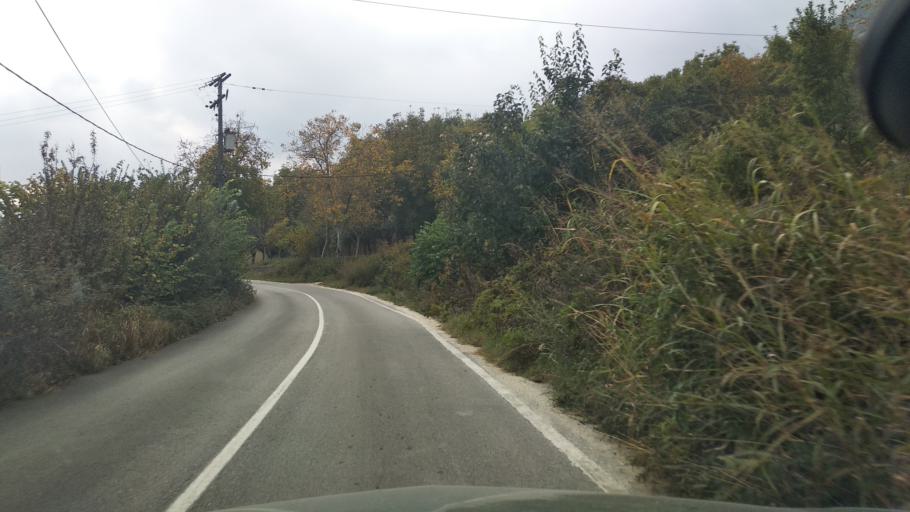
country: GR
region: Thessaly
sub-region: Trikala
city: Kastraki
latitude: 39.6783
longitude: 21.5109
